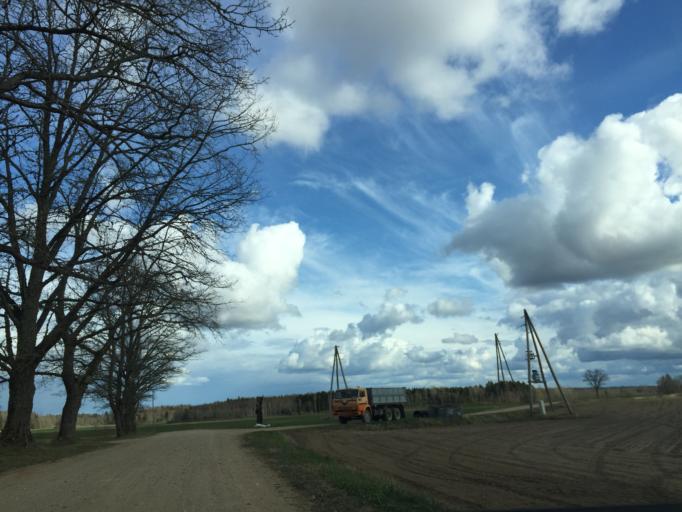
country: LV
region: Burtnieki
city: Matisi
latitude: 57.6122
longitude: 25.0221
